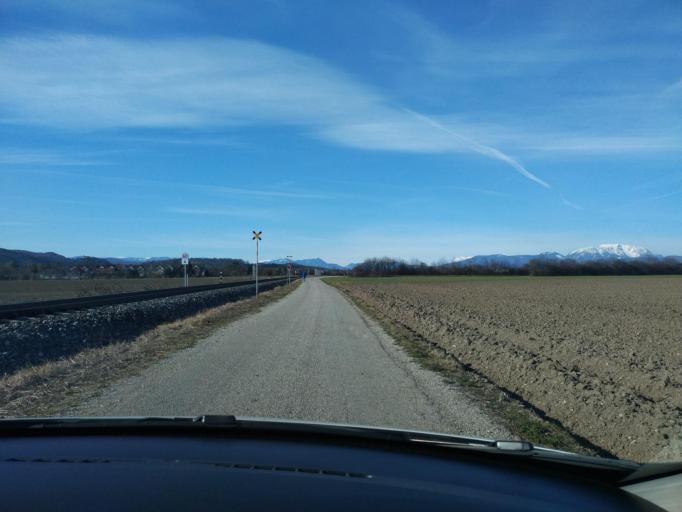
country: AT
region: Lower Austria
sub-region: Politischer Bezirk Wiener Neustadt
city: Lanzenkirchen
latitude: 47.7402
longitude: 16.2226
